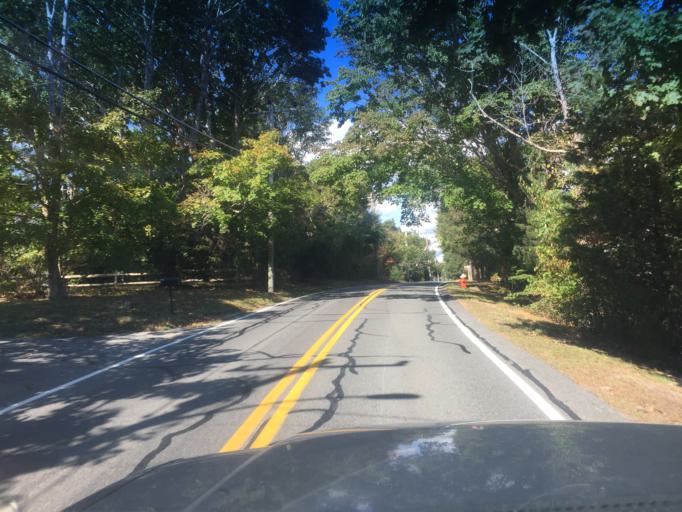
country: US
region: Massachusetts
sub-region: Barnstable County
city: Pocasset
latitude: 41.6811
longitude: -70.6141
